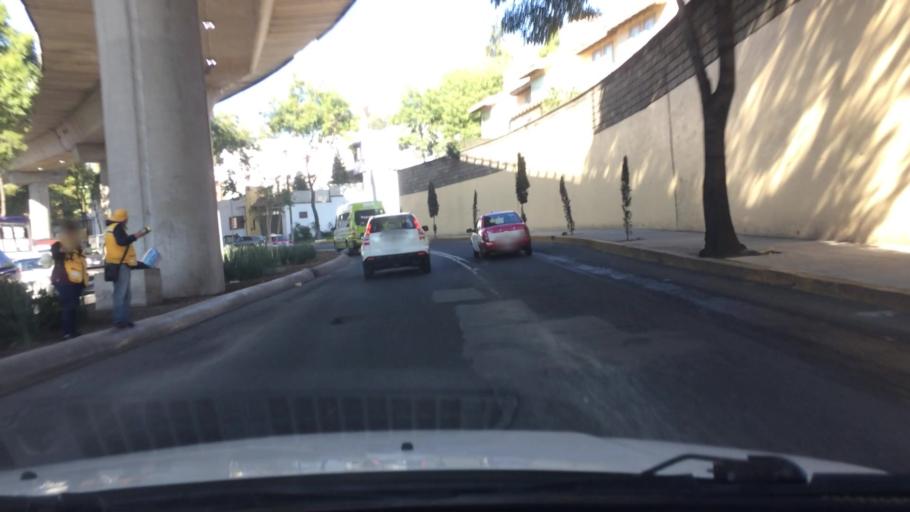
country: MX
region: Mexico City
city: Magdalena Contreras
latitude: 19.3191
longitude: -99.2297
